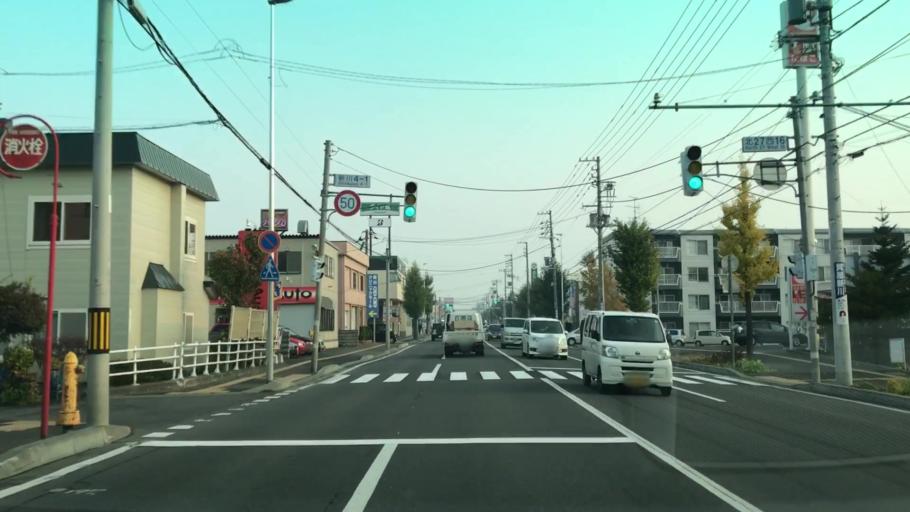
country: JP
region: Hokkaido
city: Sapporo
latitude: 43.0973
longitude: 141.3243
